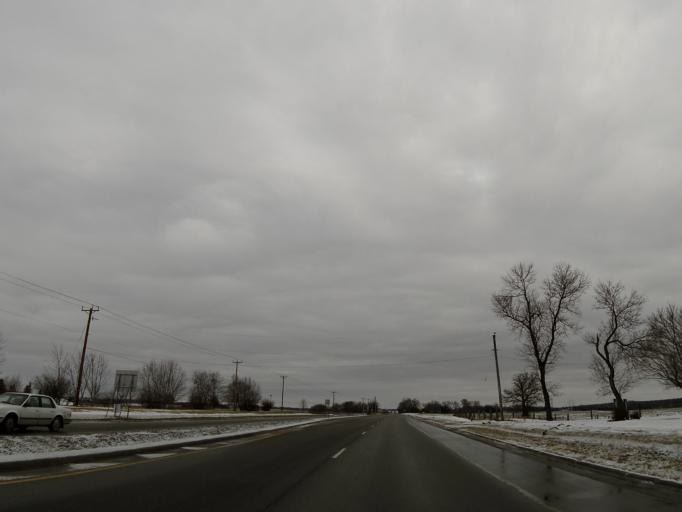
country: US
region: Minnesota
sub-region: Washington County
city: Woodbury
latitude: 44.8890
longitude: -92.9034
